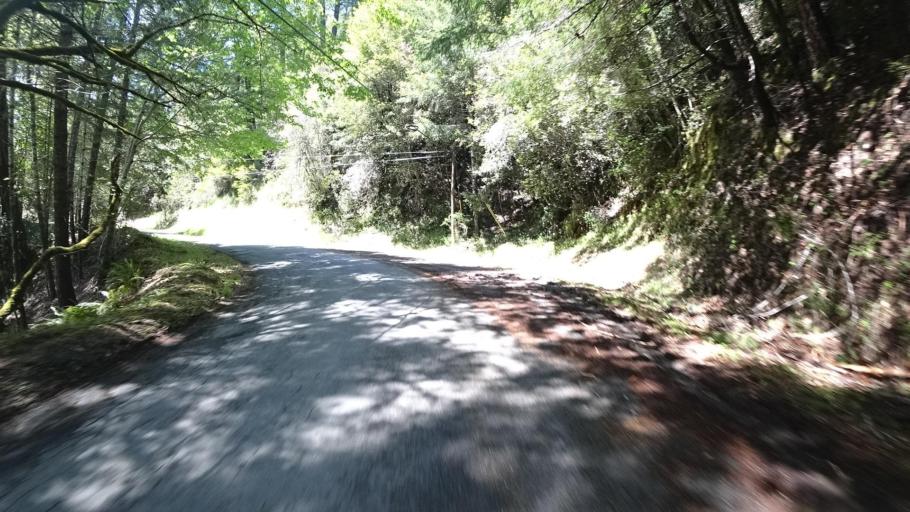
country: US
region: California
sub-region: Humboldt County
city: Blue Lake
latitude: 40.7620
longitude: -123.9544
